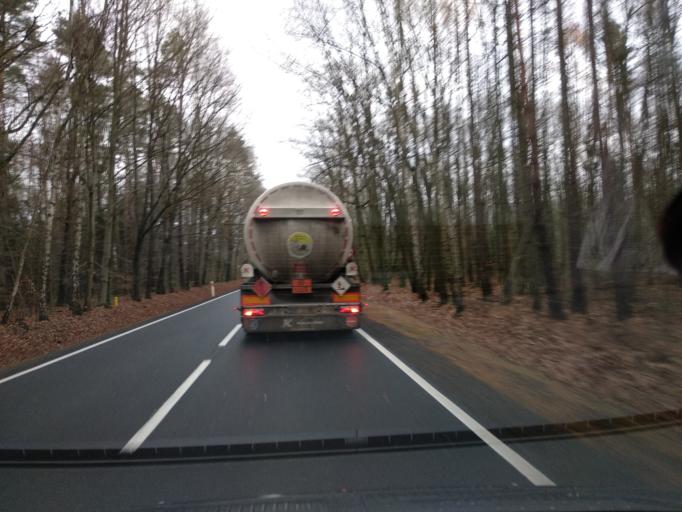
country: PL
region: Lower Silesian Voivodeship
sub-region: Powiat olesnicki
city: Twardogora
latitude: 51.3250
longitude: 17.5736
